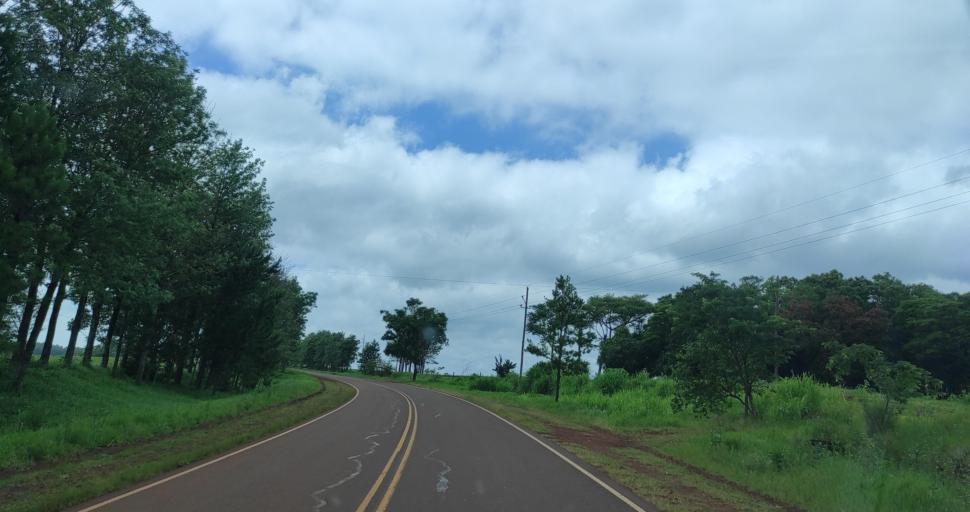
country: AR
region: Misiones
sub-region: Departamento de Veinticinco de Mayo
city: Veinticinco de Mayo
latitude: -27.4047
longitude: -54.7499
